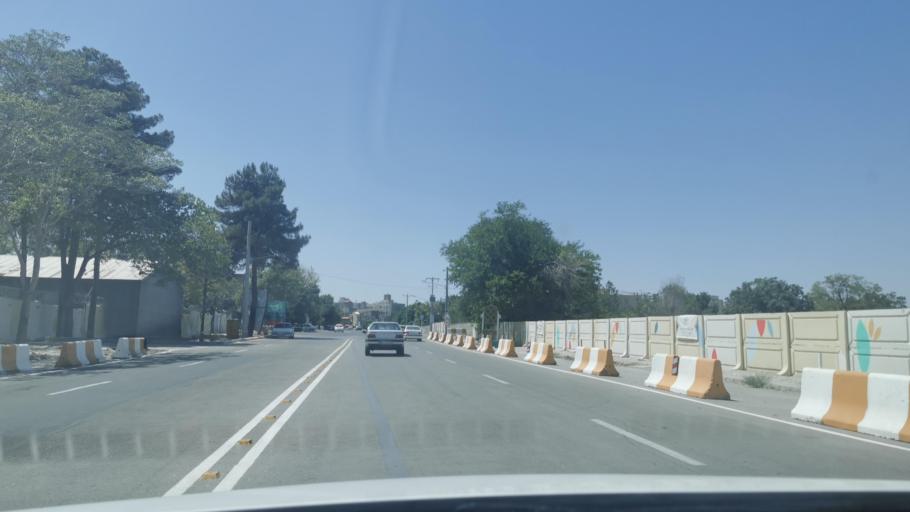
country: IR
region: Razavi Khorasan
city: Mashhad
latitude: 36.2747
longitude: 59.5802
